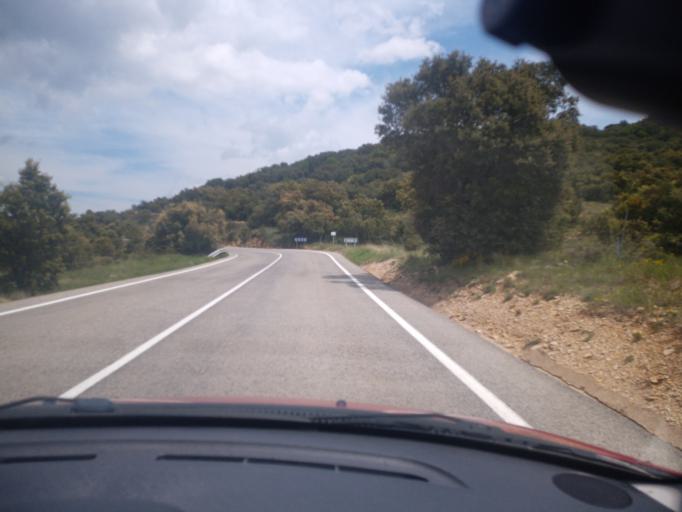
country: ES
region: Valencia
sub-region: Provincia de Castello
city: Ares del Maestre
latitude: 40.4569
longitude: -0.1603
